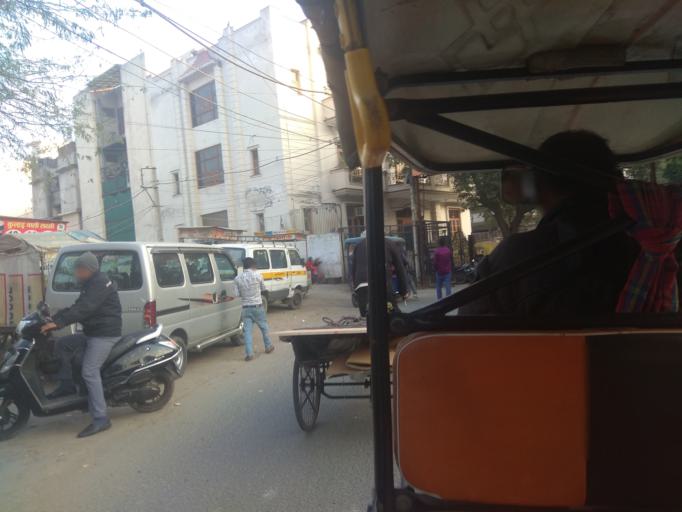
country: IN
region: NCT
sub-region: West Delhi
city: Nangloi Jat
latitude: 28.6319
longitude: 77.0764
